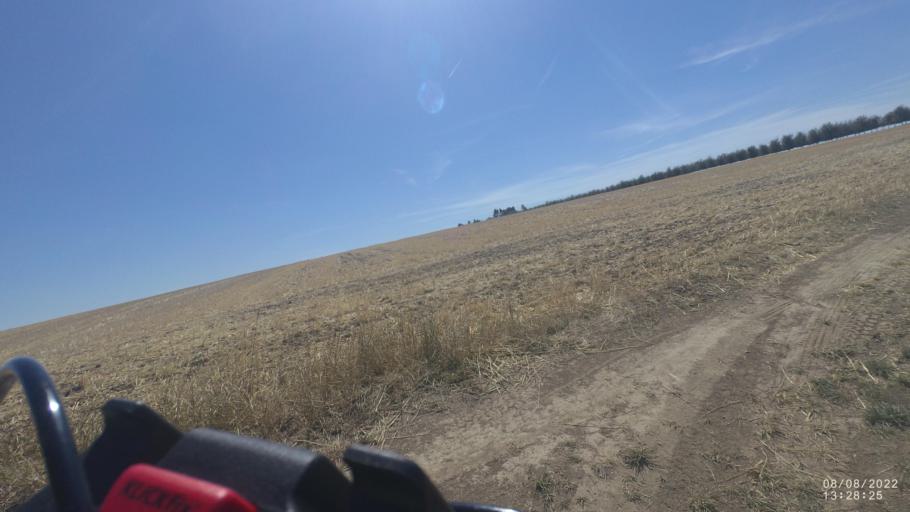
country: DE
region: Rheinland-Pfalz
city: Partenheim
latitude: 49.8741
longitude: 8.0957
